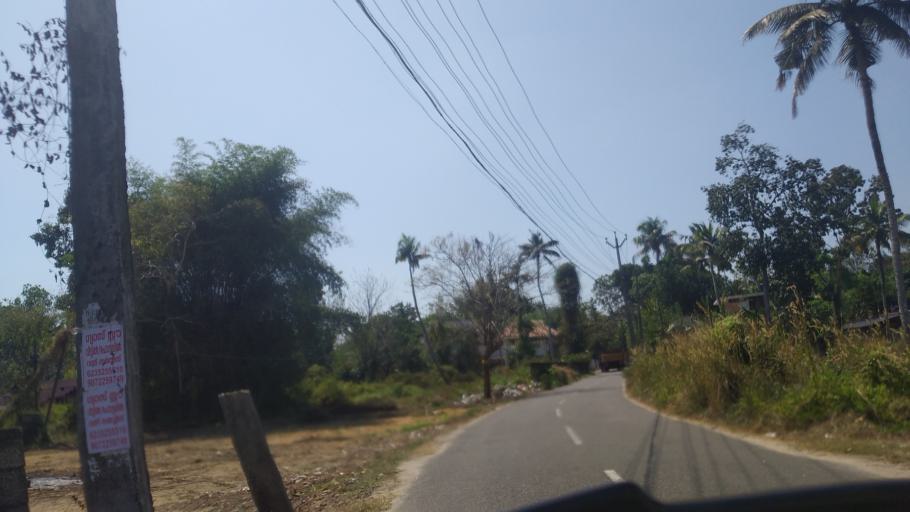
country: IN
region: Kerala
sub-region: Ernakulam
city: Elur
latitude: 10.1303
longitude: 76.2319
